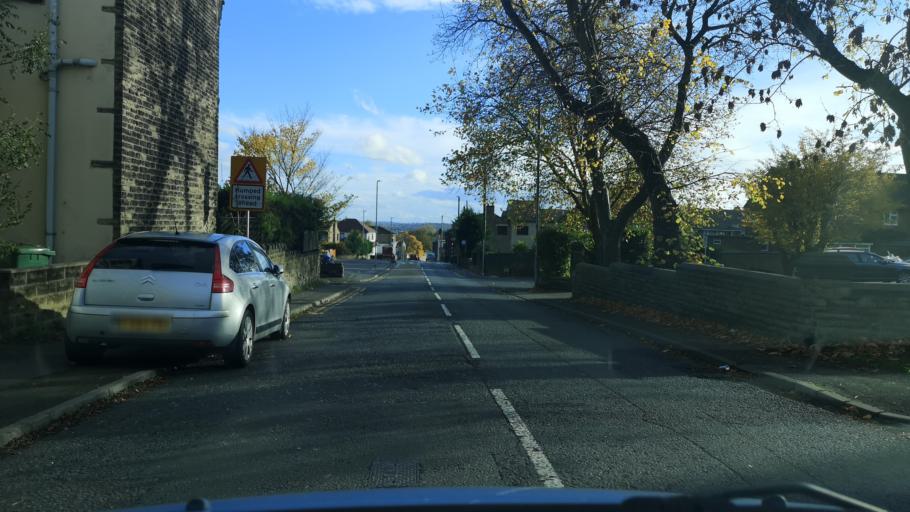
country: GB
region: England
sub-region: Kirklees
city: Batley
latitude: 53.7005
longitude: -1.6543
